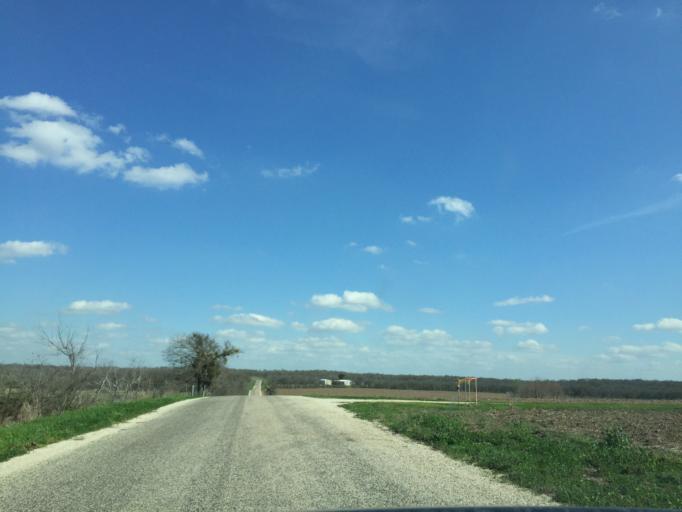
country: US
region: Texas
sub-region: Milam County
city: Thorndale
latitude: 30.5970
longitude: -97.1701
